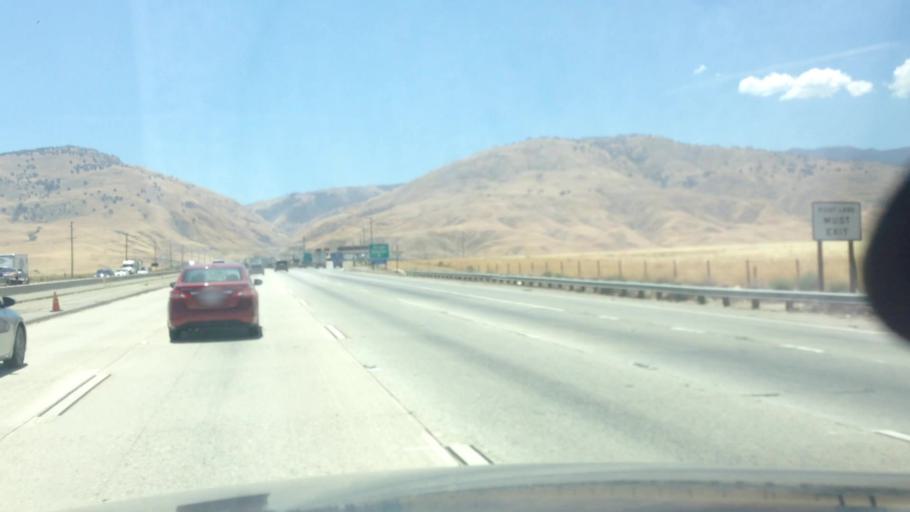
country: US
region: California
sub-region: Kern County
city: Frazier Park
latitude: 34.9649
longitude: -118.9389
